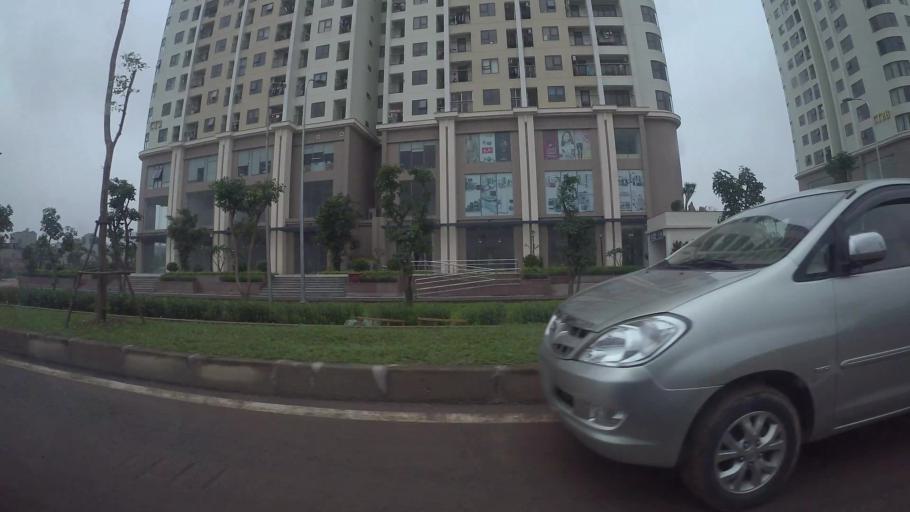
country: VN
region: Ha Noi
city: Van Dien
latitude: 20.9746
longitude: 105.8706
